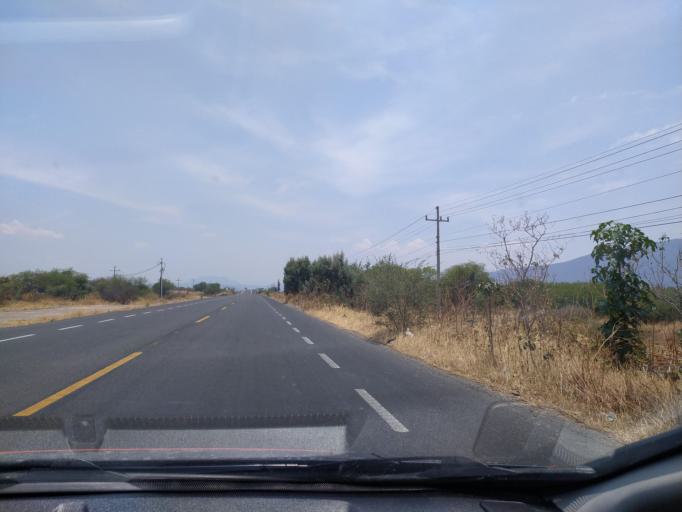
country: MX
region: Jalisco
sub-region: Acatlan de Juarez
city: Villa de los Ninos
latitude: 20.3336
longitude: -103.5907
